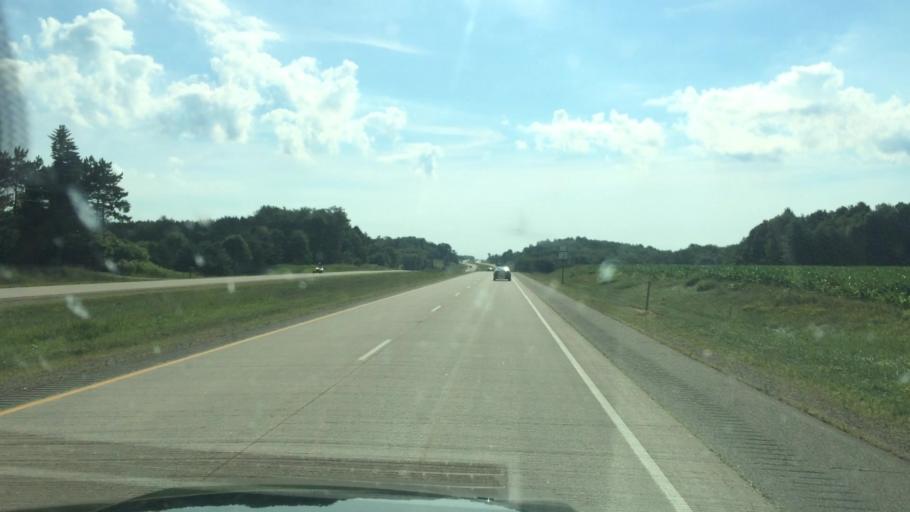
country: US
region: Wisconsin
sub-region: Shawano County
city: Wittenberg
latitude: 44.8036
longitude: -89.0256
